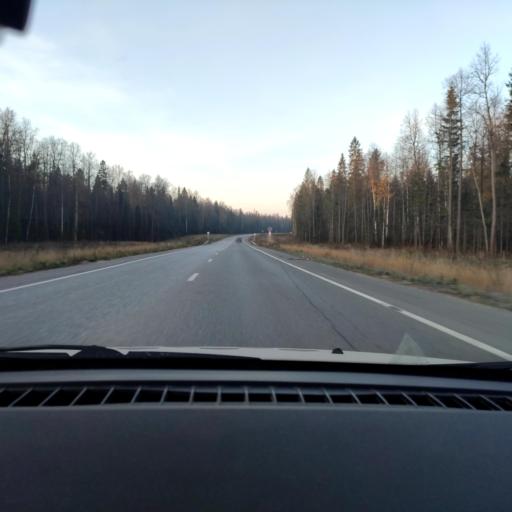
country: RU
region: Perm
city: Novyye Lyady
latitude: 58.0349
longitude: 56.5330
